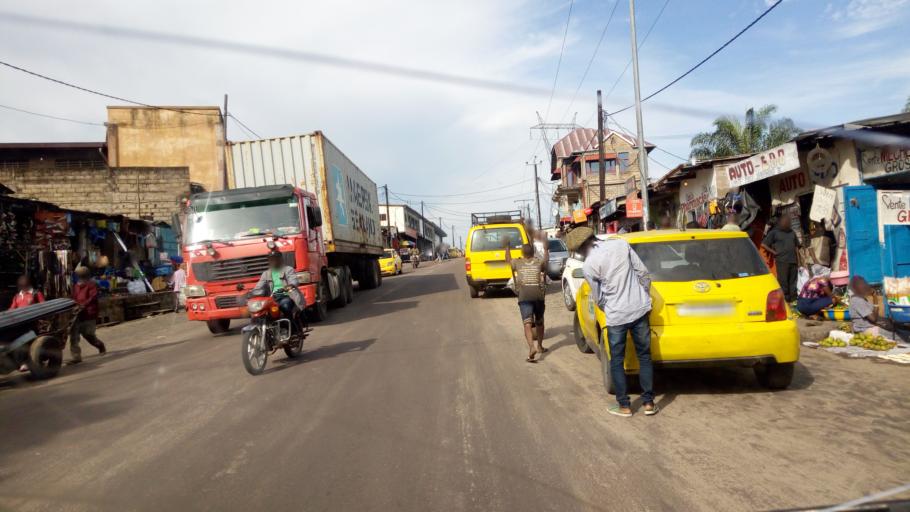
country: CD
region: Kinshasa
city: Kinshasa
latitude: -4.4457
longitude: 15.2512
